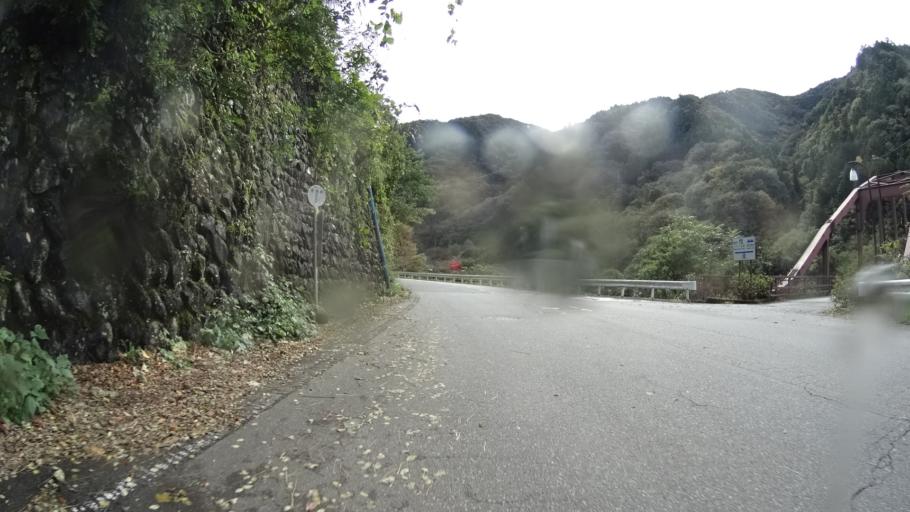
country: JP
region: Yamanashi
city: Otsuki
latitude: 35.7801
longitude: 138.9794
